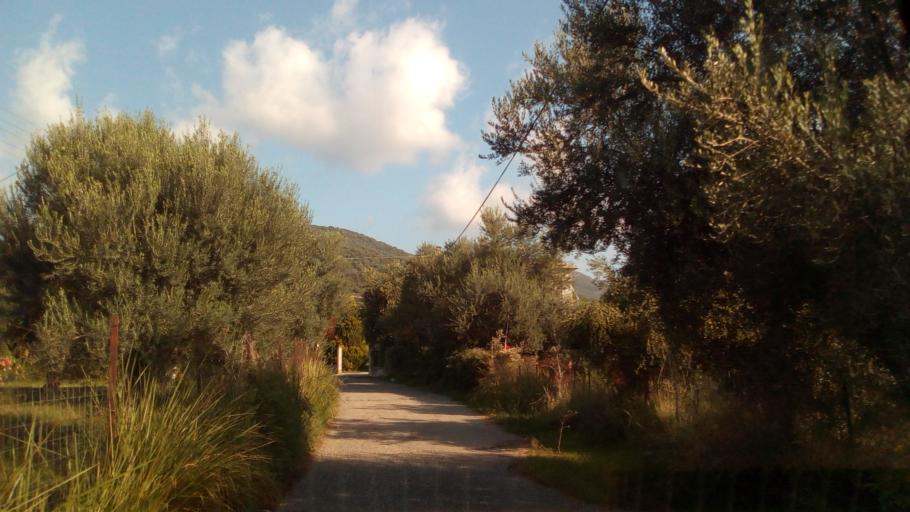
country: GR
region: West Greece
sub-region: Nomos Aitolias kai Akarnanias
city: Nafpaktos
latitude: 38.4147
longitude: 21.8891
